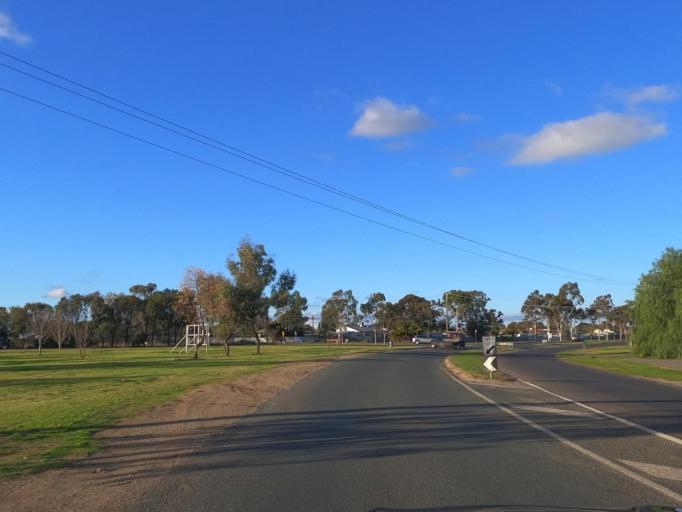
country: AU
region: Victoria
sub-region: Swan Hill
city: Swan Hill
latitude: -35.3400
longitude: 143.5393
